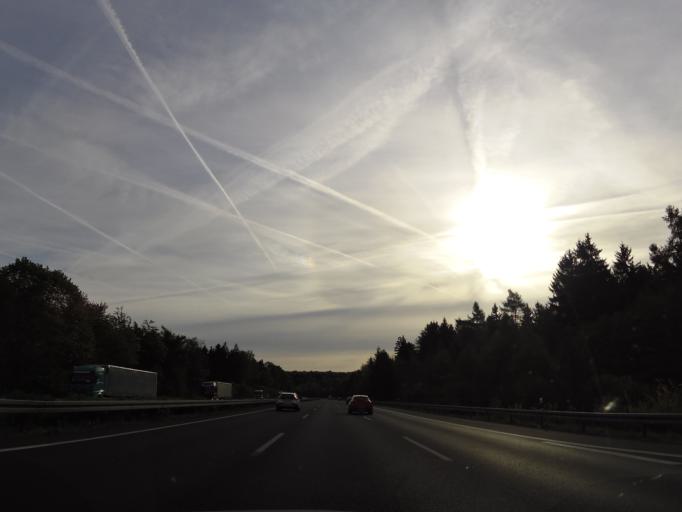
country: DE
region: Lower Saxony
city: Hannoversch Munden
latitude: 51.3705
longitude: 9.6432
